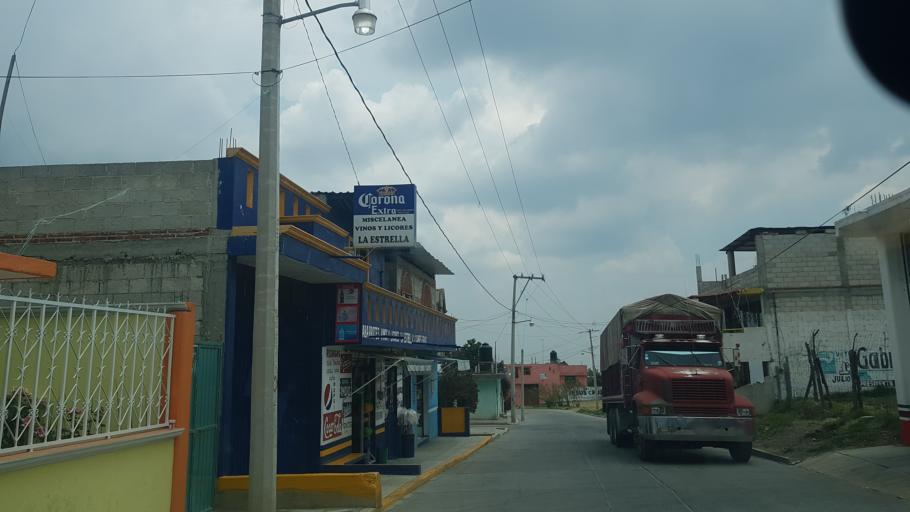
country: MX
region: Puebla
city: Domingo Arenas
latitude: 19.1506
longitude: -98.4954
